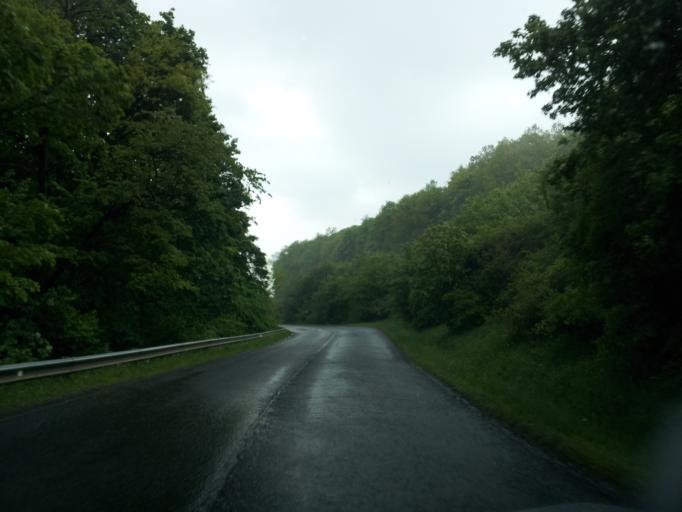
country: HU
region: Baranya
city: Hosszuheteny
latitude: 46.1703
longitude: 18.3326
